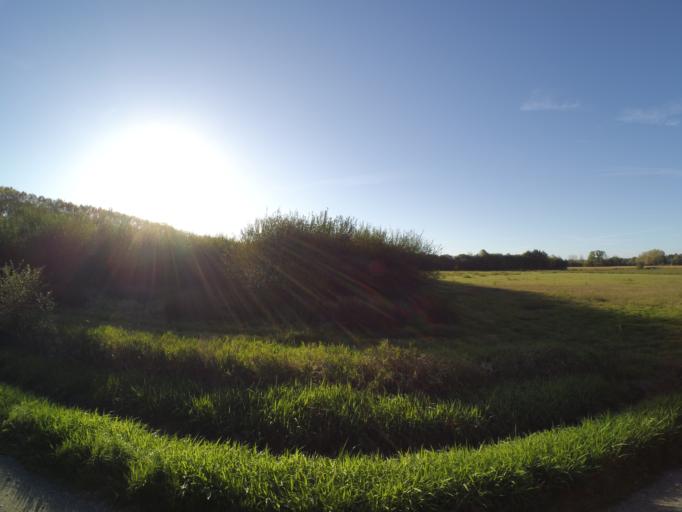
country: FR
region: Brittany
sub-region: Departement du Morbihan
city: Saint-Vincent-sur-Oust
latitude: 47.7223
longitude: -2.1689
